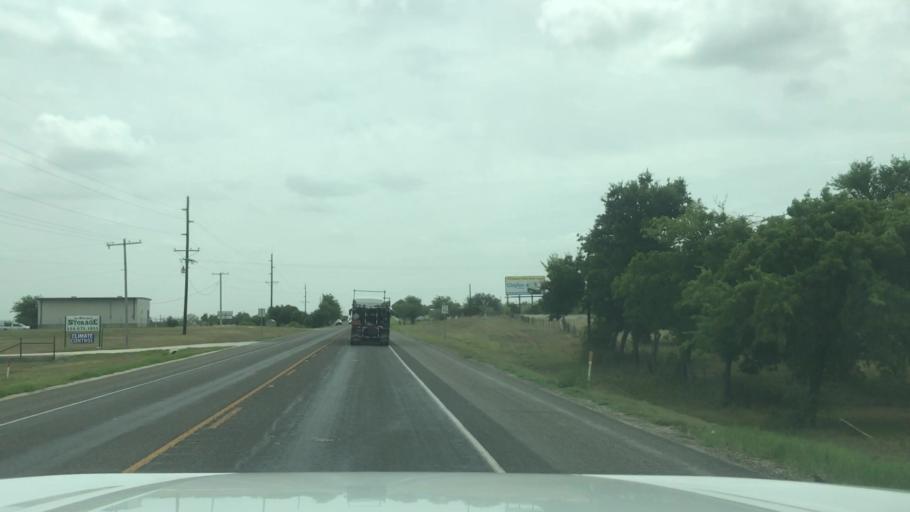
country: US
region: Texas
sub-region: Bosque County
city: Clifton
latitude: 31.7637
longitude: -97.5654
